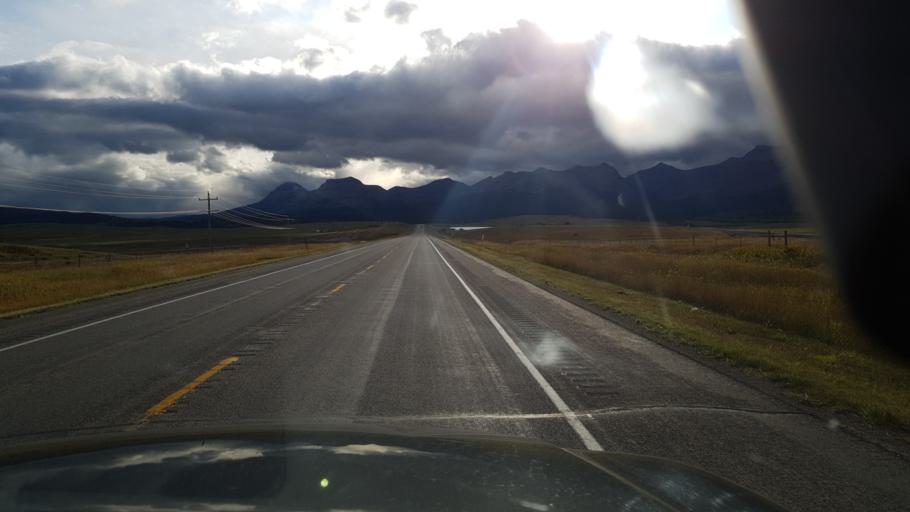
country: US
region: Montana
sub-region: Glacier County
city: South Browning
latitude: 48.4594
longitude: -113.1757
